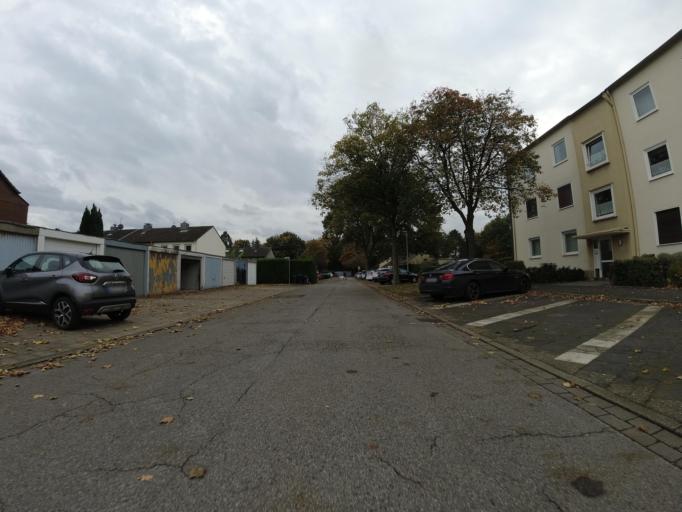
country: DE
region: North Rhine-Westphalia
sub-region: Regierungsbezirk Dusseldorf
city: Hochfeld
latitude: 51.4148
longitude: 6.6958
